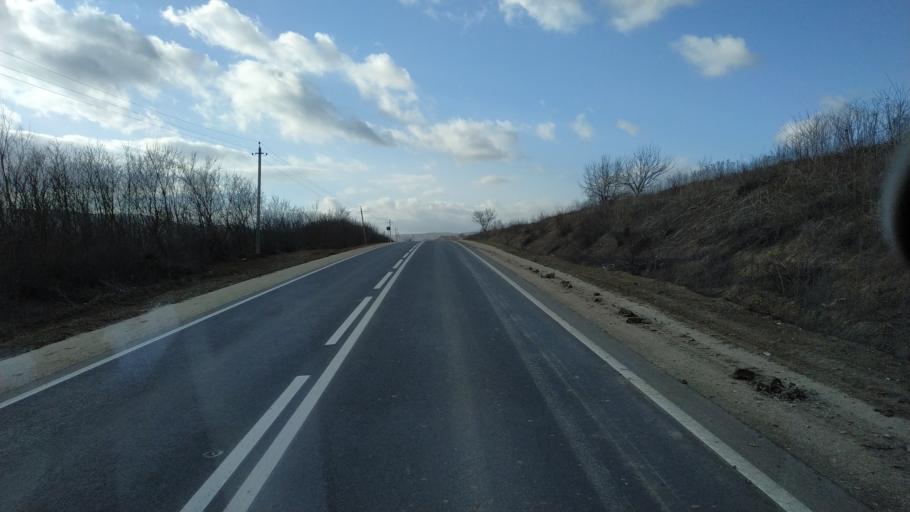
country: MD
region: Calarasi
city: Calarasi
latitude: 47.2917
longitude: 28.1783
